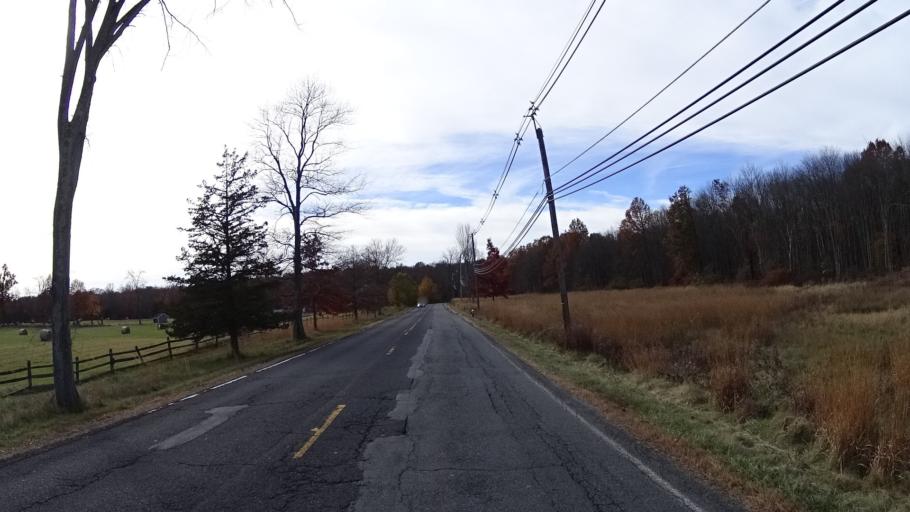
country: US
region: New Jersey
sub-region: Morris County
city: Madison
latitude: 40.7531
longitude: -74.4444
